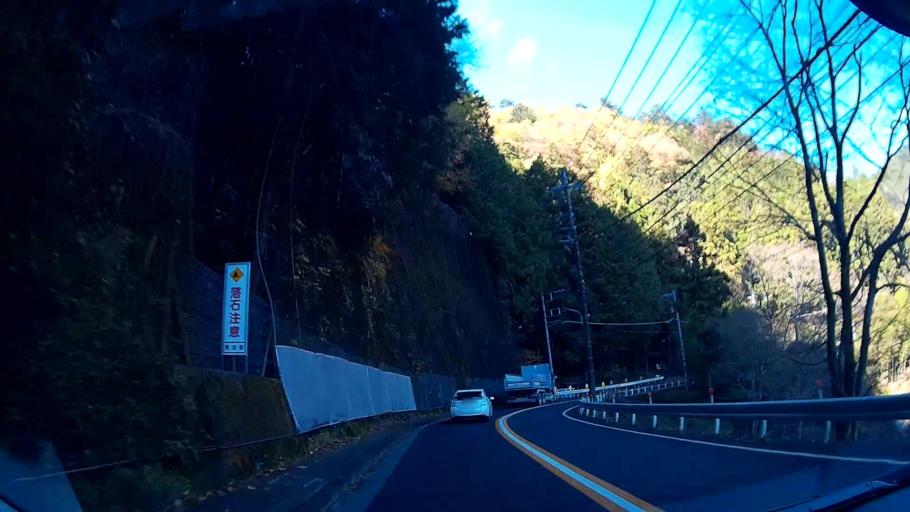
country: JP
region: Tokyo
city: Itsukaichi
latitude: 35.7239
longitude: 139.1592
